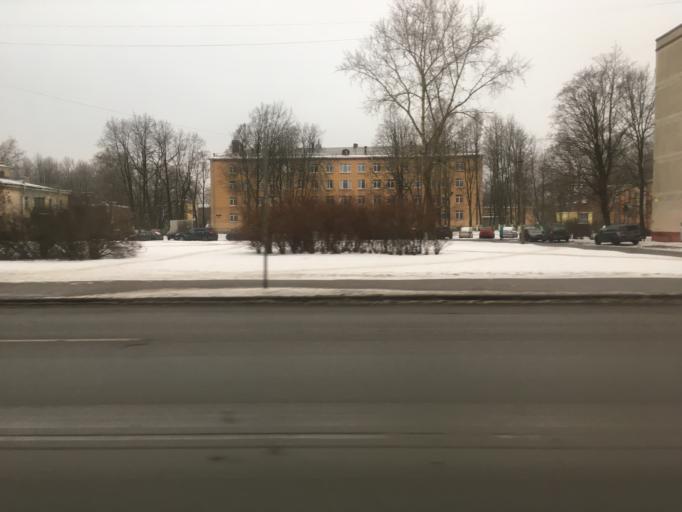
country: RU
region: St.-Petersburg
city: Obukhovo
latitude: 59.8668
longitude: 30.4432
